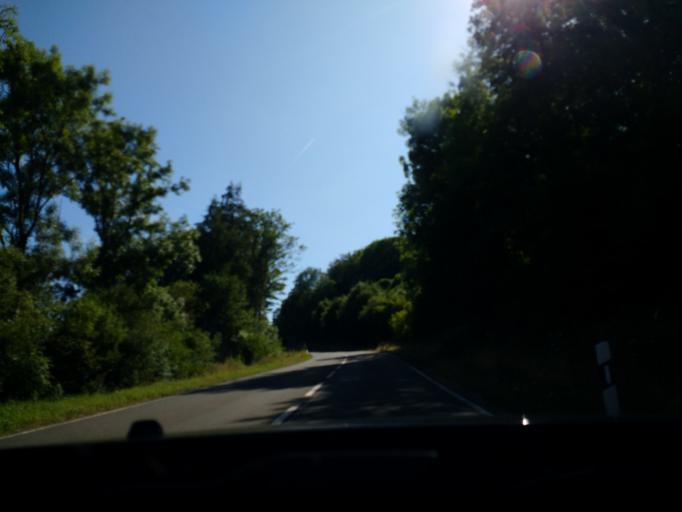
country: DE
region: Rheinland-Pfalz
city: Udersdorf
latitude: 50.1562
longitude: 6.8160
